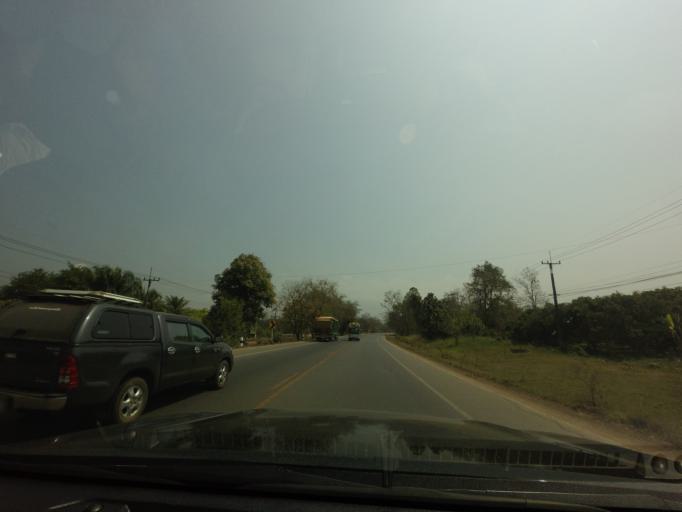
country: TH
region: Kanchanaburi
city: Thong Pha Phum
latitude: 14.6458
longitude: 98.6986
